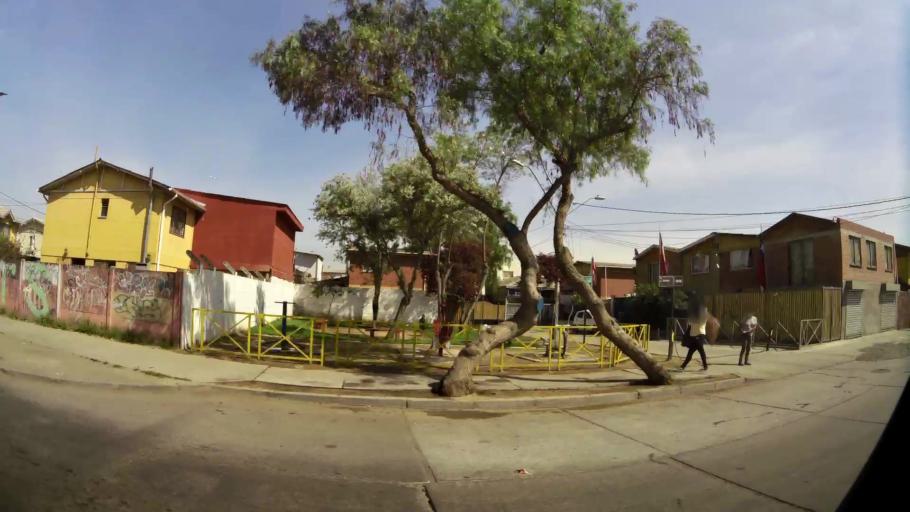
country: CL
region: Santiago Metropolitan
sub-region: Provincia de Santiago
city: Lo Prado
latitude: -33.4342
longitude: -70.7708
